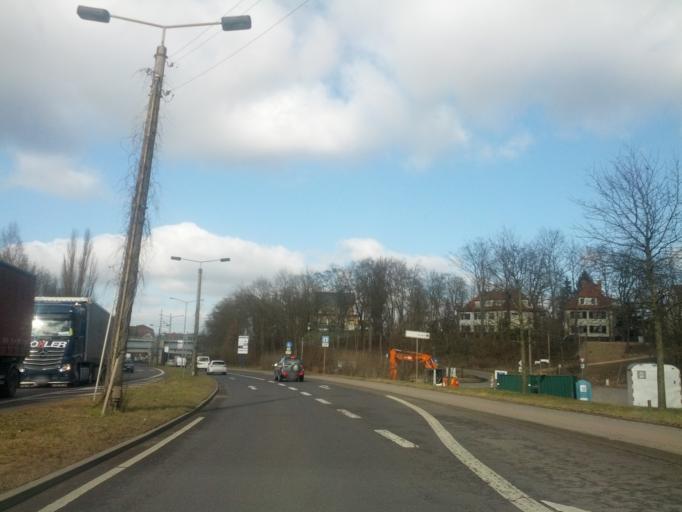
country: DE
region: Thuringia
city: Gotha
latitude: 50.9358
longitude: 10.7169
